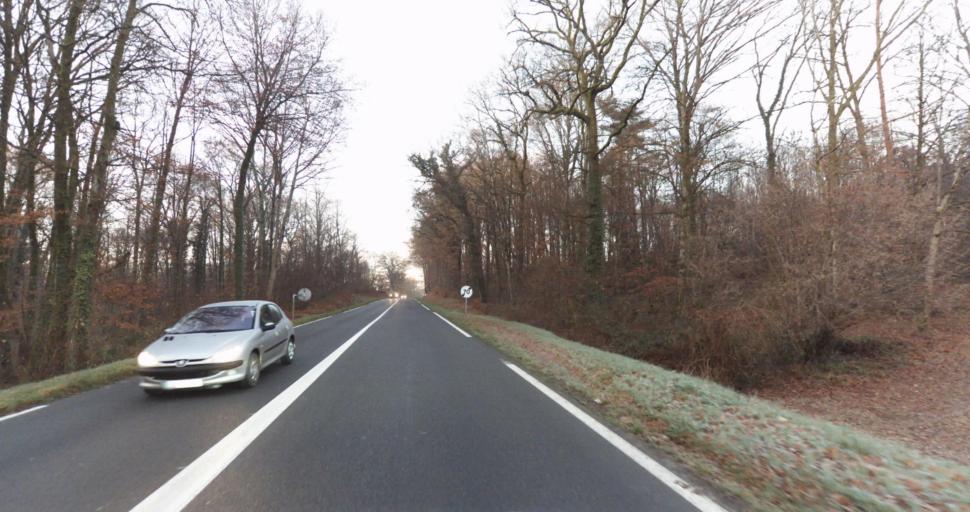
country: FR
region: Limousin
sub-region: Departement de la Haute-Vienne
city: Aixe-sur-Vienne
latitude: 45.8147
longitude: 1.1706
